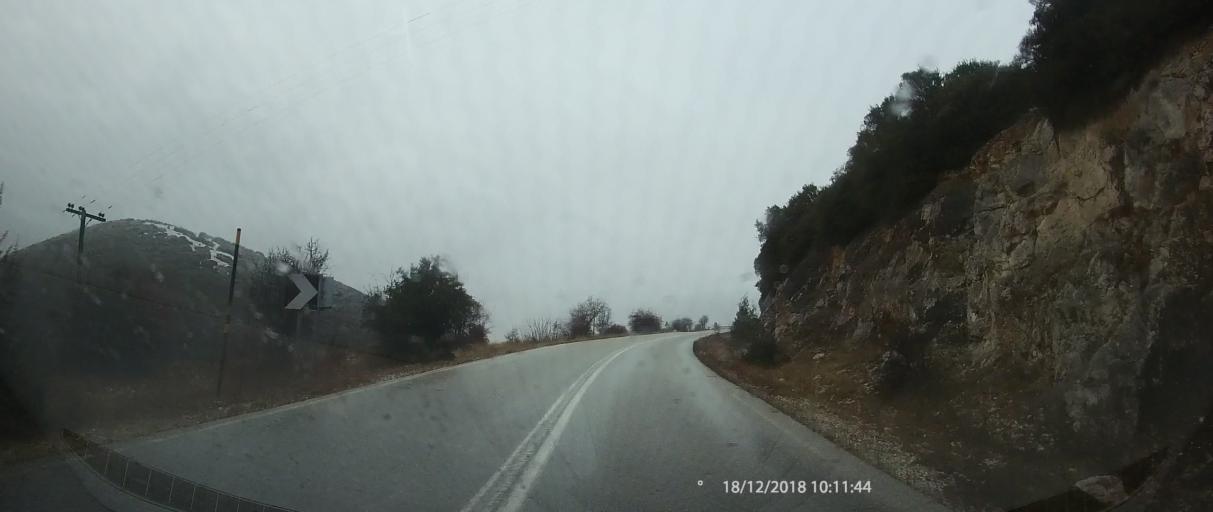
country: GR
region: Thessaly
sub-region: Nomos Larisis
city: Livadi
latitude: 40.0938
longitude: 22.2089
